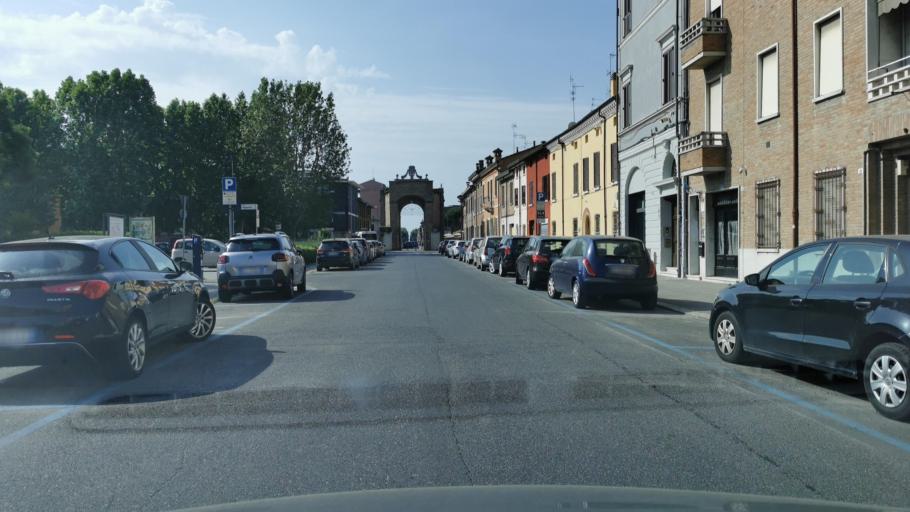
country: IT
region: Emilia-Romagna
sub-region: Provincia di Ravenna
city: Ravenna
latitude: 44.4133
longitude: 12.2059
